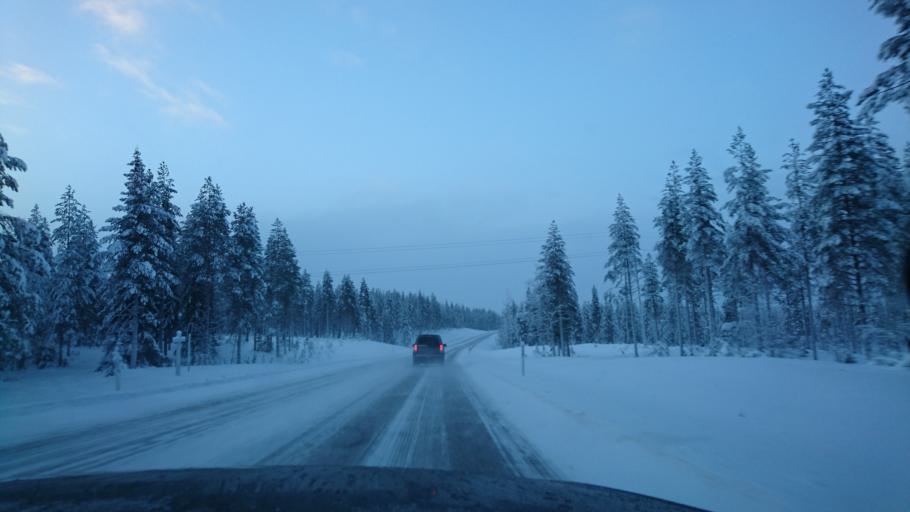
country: FI
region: Northern Ostrobothnia
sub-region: Koillismaa
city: Taivalkoski
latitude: 65.4702
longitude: 27.7300
